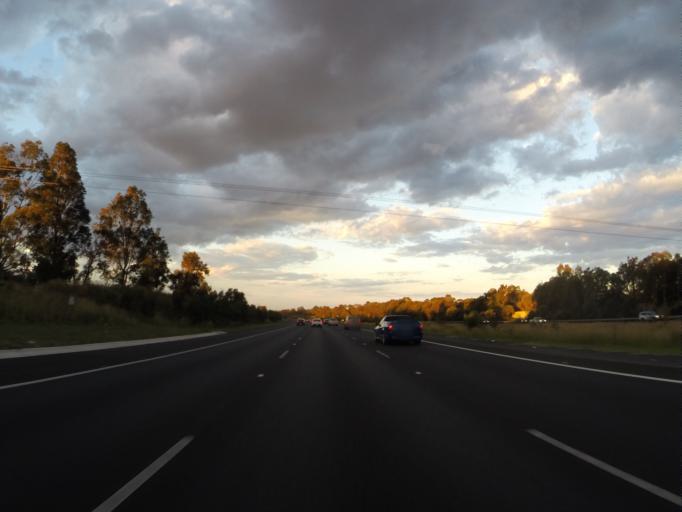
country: AU
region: New South Wales
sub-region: Campbelltown Municipality
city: Campbelltown
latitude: -34.0511
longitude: 150.8124
